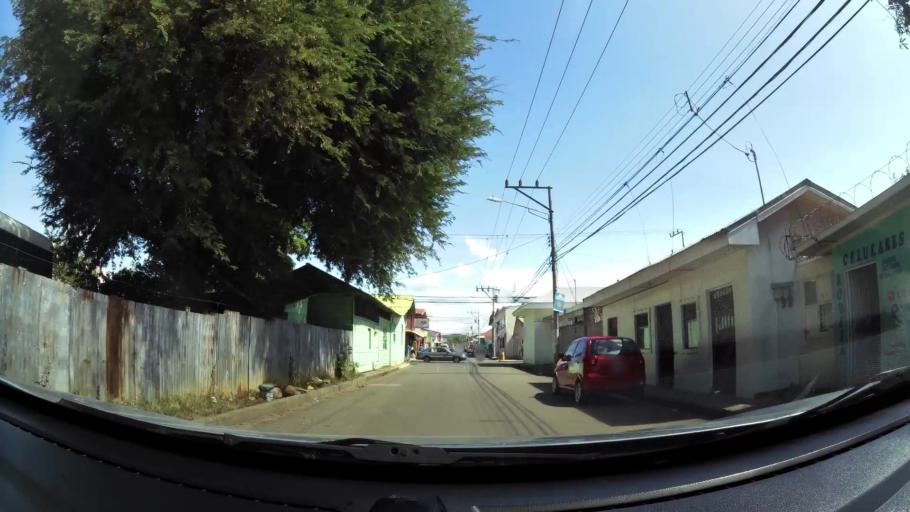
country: CR
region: Guanacaste
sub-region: Canton de Canas
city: Canas
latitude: 10.4271
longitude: -85.0927
